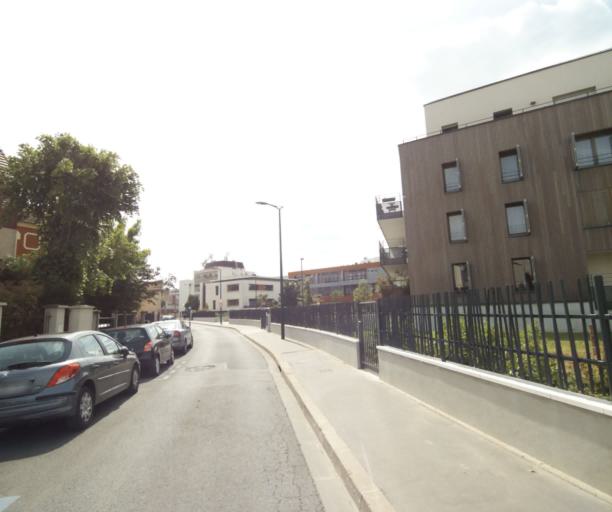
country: FR
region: Ile-de-France
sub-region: Departement des Hauts-de-Seine
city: Colombes
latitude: 48.9288
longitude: 2.2568
